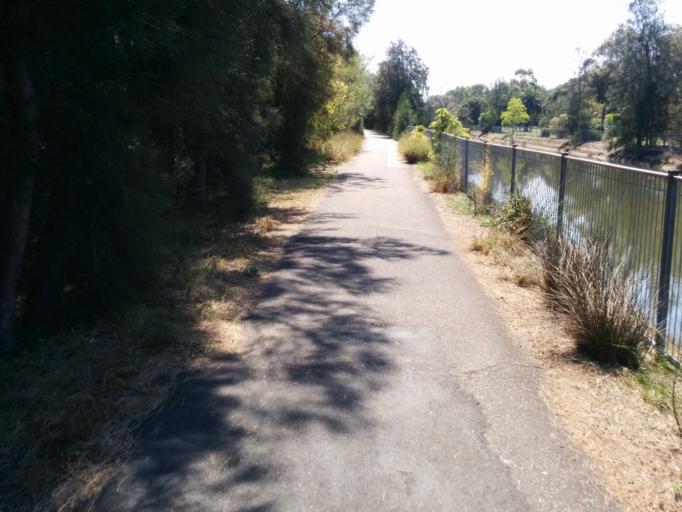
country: AU
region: New South Wales
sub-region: Canada Bay
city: Concord West
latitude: -33.8554
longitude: 151.0831
